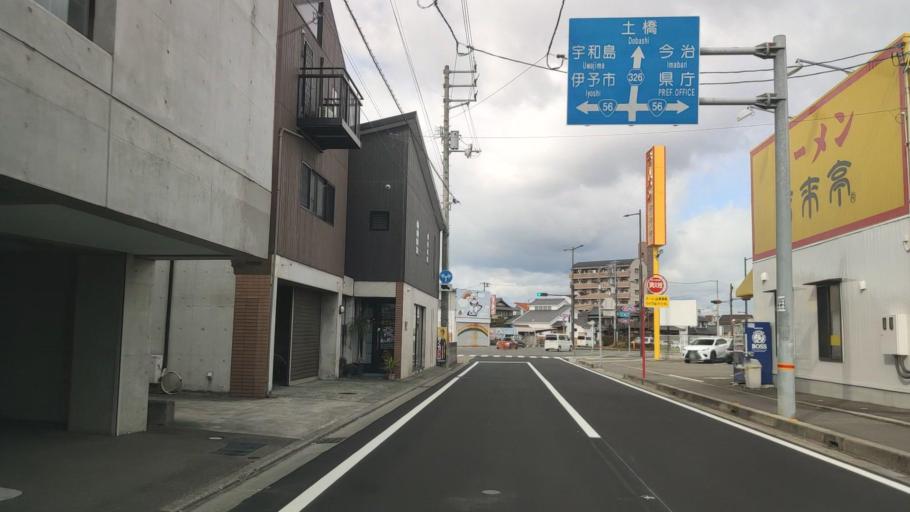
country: JP
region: Ehime
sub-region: Shikoku-chuo Shi
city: Matsuyama
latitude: 33.8229
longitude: 132.7578
